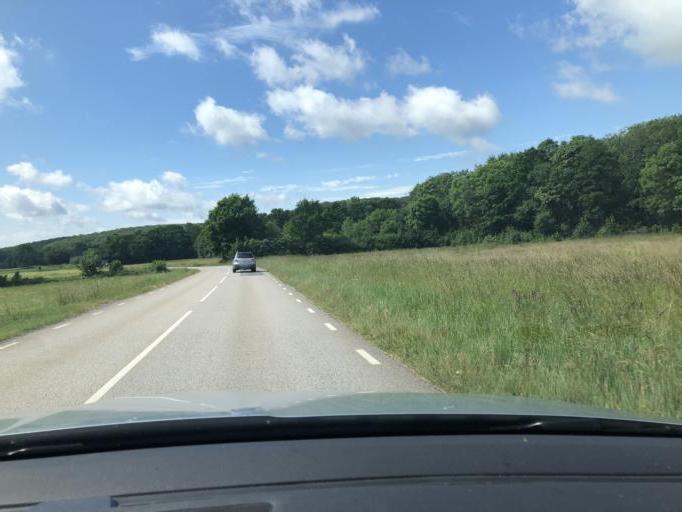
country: SE
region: Blekinge
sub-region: Solvesborgs Kommun
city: Soelvesborg
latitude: 56.0925
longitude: 14.6096
